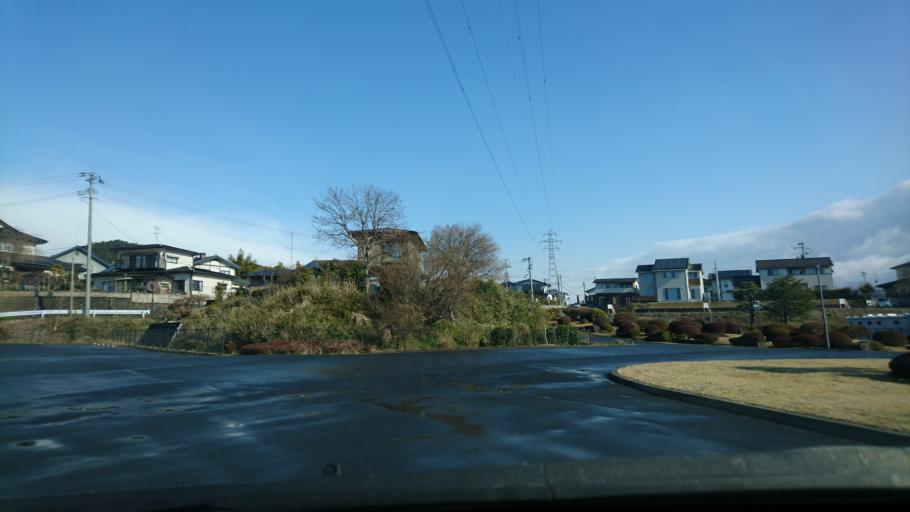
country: JP
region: Iwate
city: Ichinoseki
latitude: 38.9850
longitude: 141.1115
